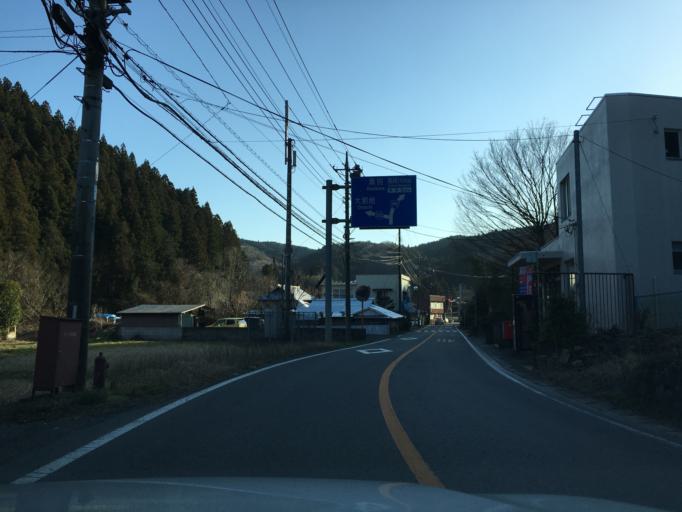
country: JP
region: Ibaraki
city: Daigo
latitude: 36.7612
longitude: 140.2225
